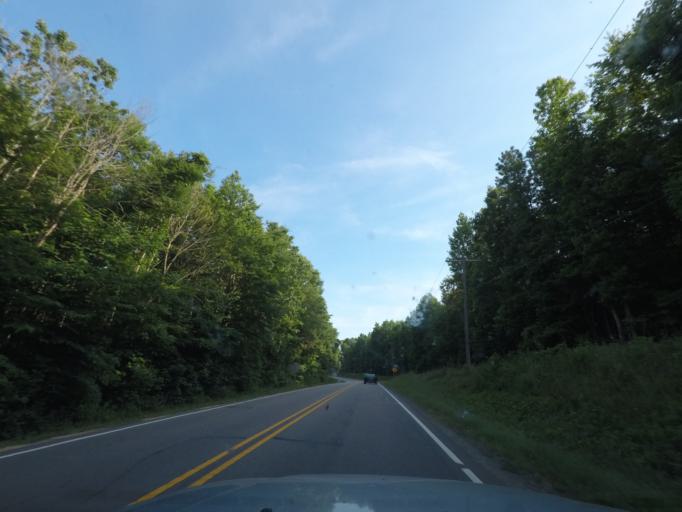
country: US
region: North Carolina
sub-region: Granville County
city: Oxford
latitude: 36.3805
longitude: -78.5944
